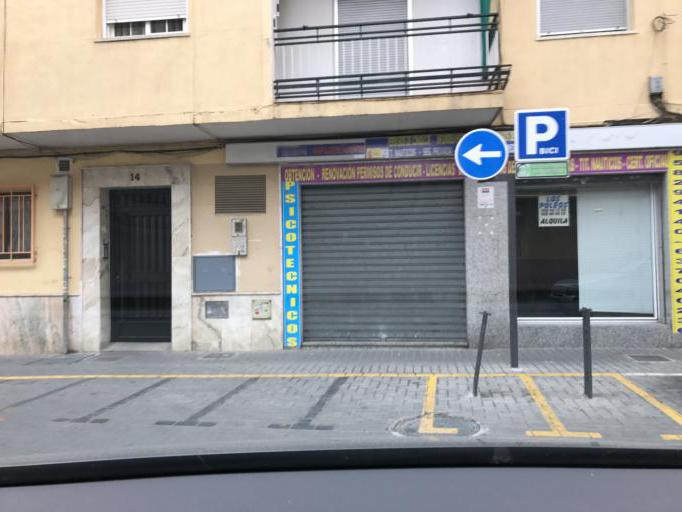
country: ES
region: Andalusia
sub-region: Provincia de Granada
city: Maracena
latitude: 37.2063
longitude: -3.6331
